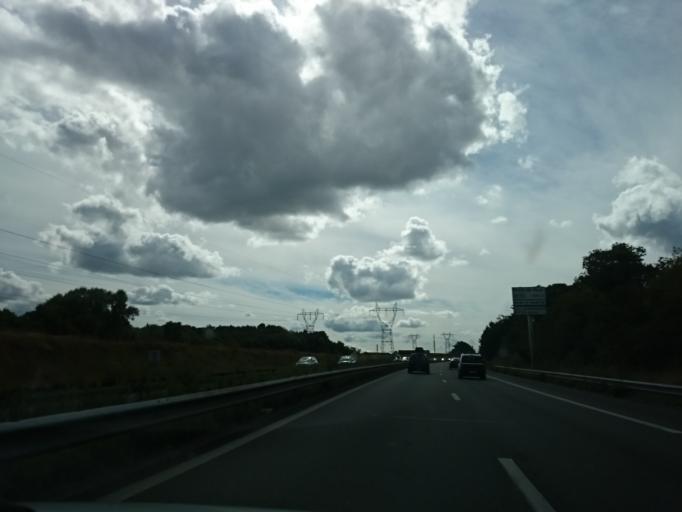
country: FR
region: Pays de la Loire
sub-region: Departement de la Loire-Atlantique
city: Les Sorinieres
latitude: 47.1626
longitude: -1.5275
